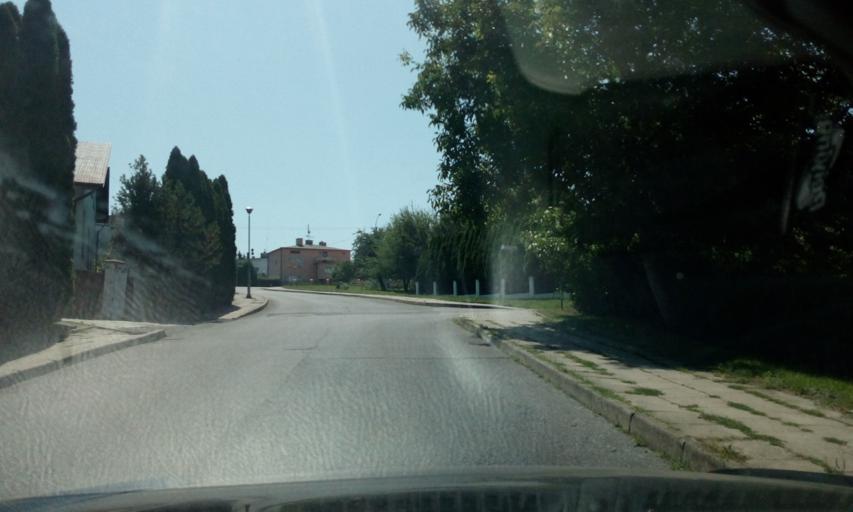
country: PL
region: Subcarpathian Voivodeship
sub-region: Powiat lancucki
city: Lancut
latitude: 50.0571
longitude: 22.2355
